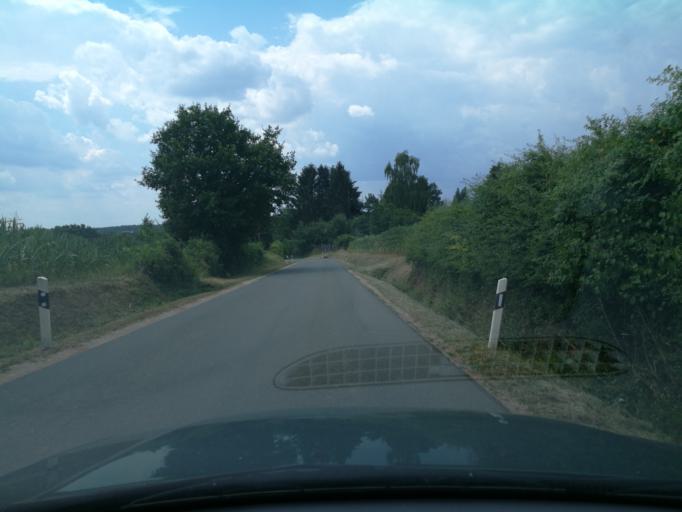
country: DE
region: Bavaria
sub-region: Regierungsbezirk Mittelfranken
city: Grosshabersdorf
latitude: 49.4140
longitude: 10.7808
